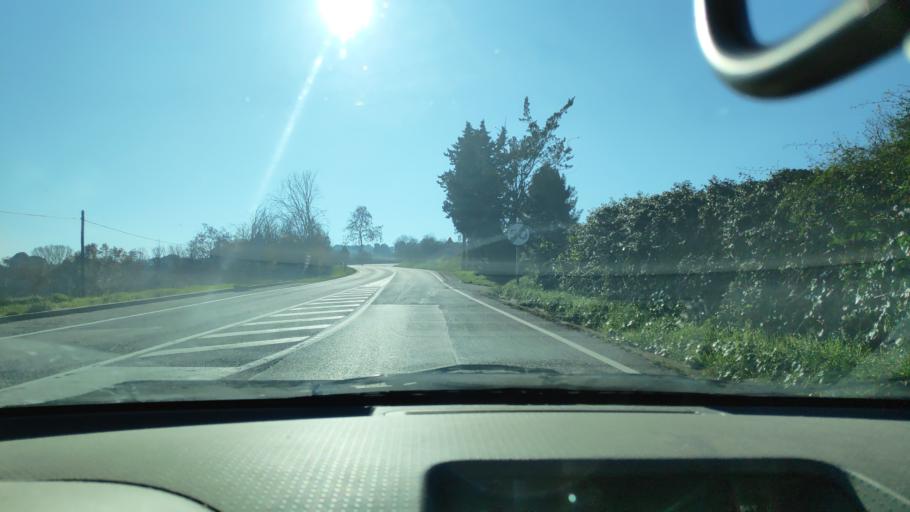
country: ES
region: Catalonia
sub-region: Provincia de Barcelona
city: Sant Quirze del Valles
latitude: 41.5257
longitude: 2.0853
